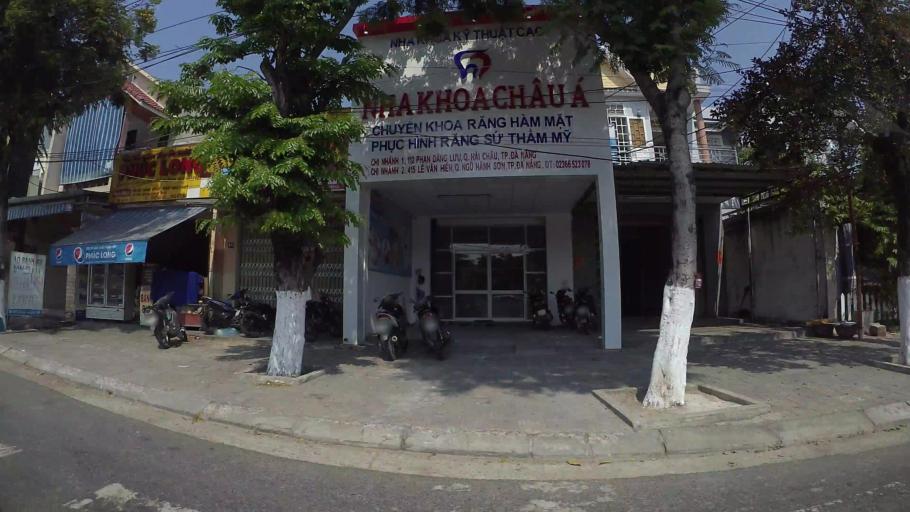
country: VN
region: Da Nang
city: Ngu Hanh Son
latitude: 16.0066
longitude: 108.2593
